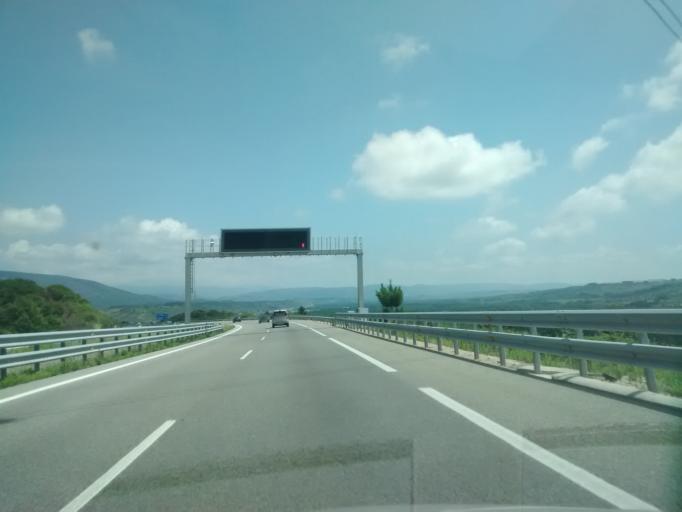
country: ES
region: Castille and Leon
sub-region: Provincia de Leon
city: Molinaseca
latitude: 42.5761
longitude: -6.5326
